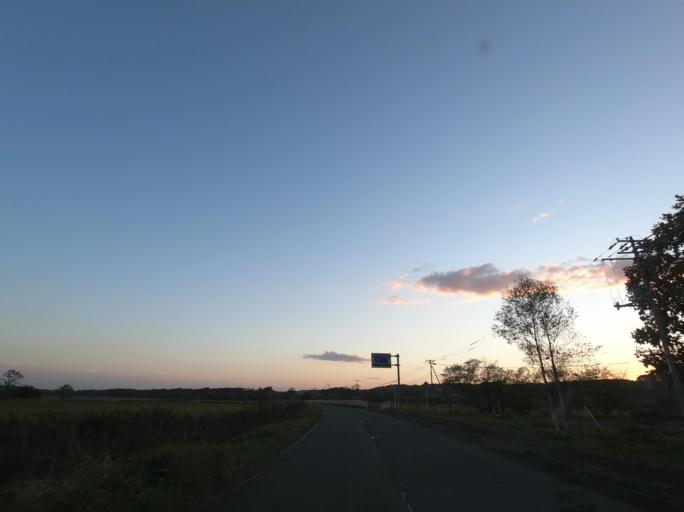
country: JP
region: Hokkaido
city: Kushiro
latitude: 43.2255
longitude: 144.4348
